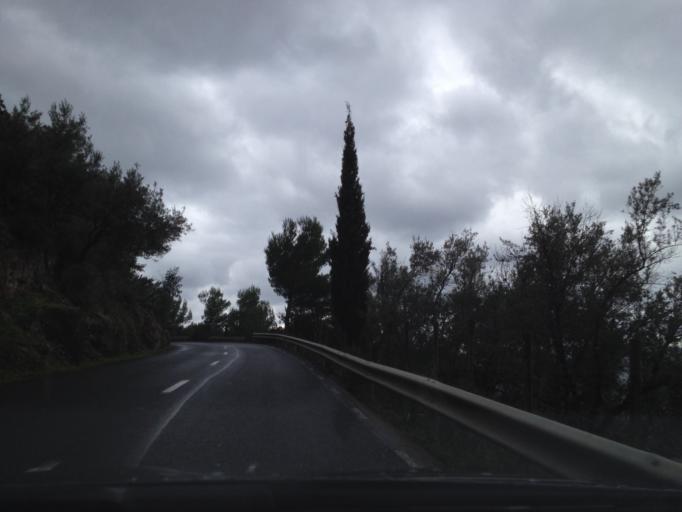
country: ES
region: Balearic Islands
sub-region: Illes Balears
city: Deia
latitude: 39.7639
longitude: 2.6542
